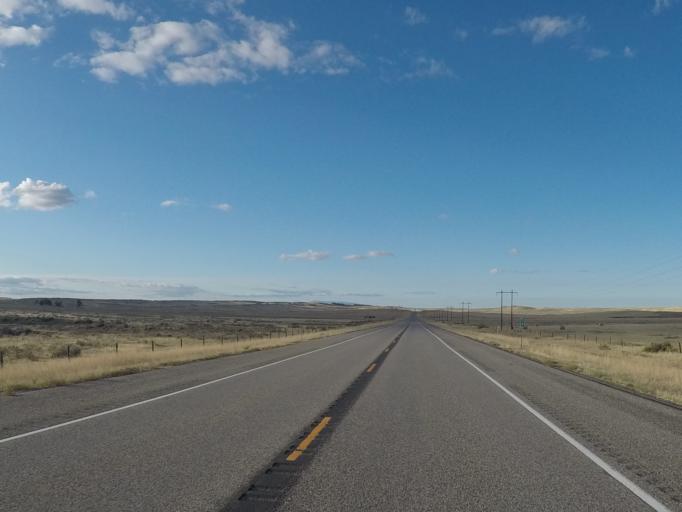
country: US
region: Montana
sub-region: Golden Valley County
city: Ryegate
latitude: 46.1978
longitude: -108.9176
